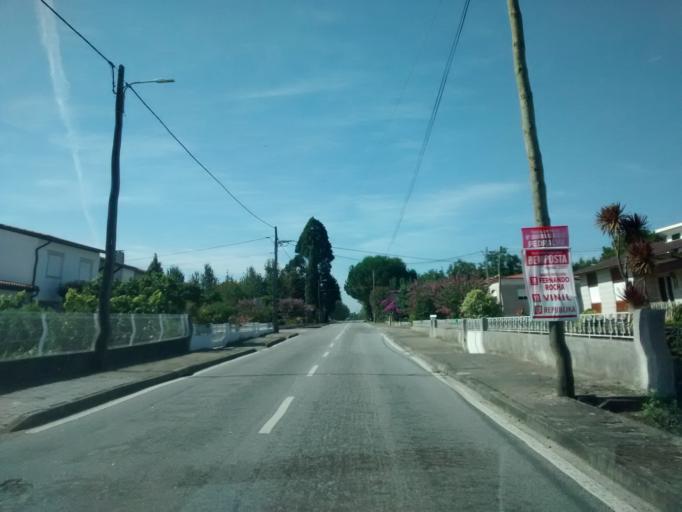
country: PT
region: Aveiro
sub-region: Anadia
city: Sangalhos
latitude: 40.4278
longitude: -8.5137
